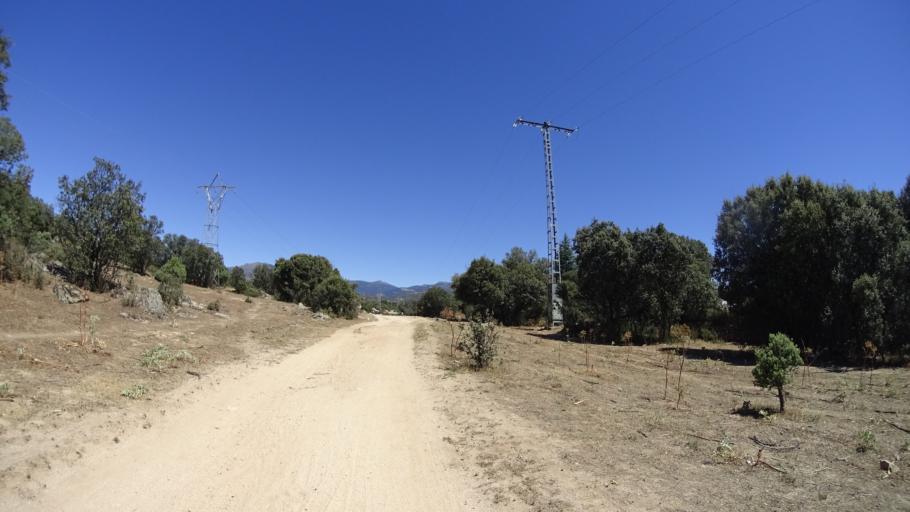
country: ES
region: Madrid
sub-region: Provincia de Madrid
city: Alpedrete
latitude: 40.6580
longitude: -4.0477
